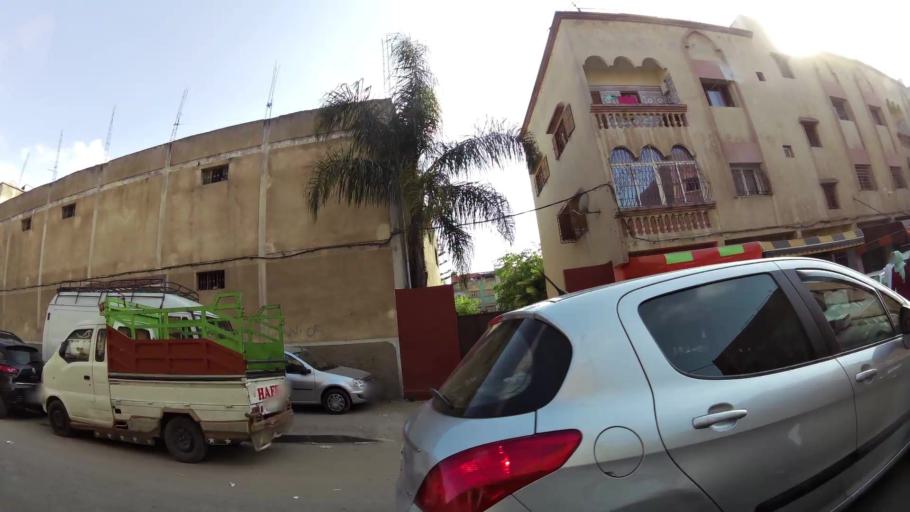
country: MA
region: Rabat-Sale-Zemmour-Zaer
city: Sale
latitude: 34.0513
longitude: -6.7790
